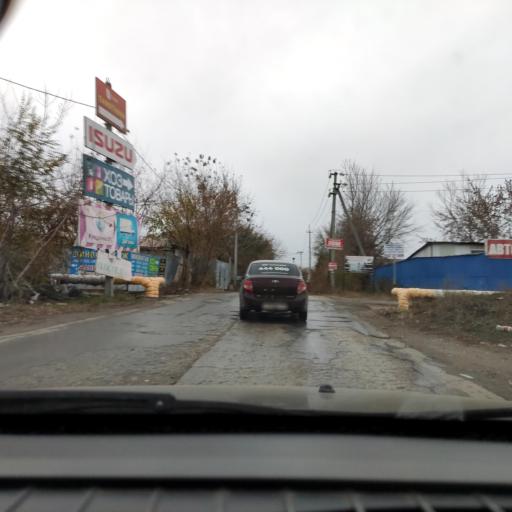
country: RU
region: Samara
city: Tol'yatti
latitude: 53.5346
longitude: 49.2621
